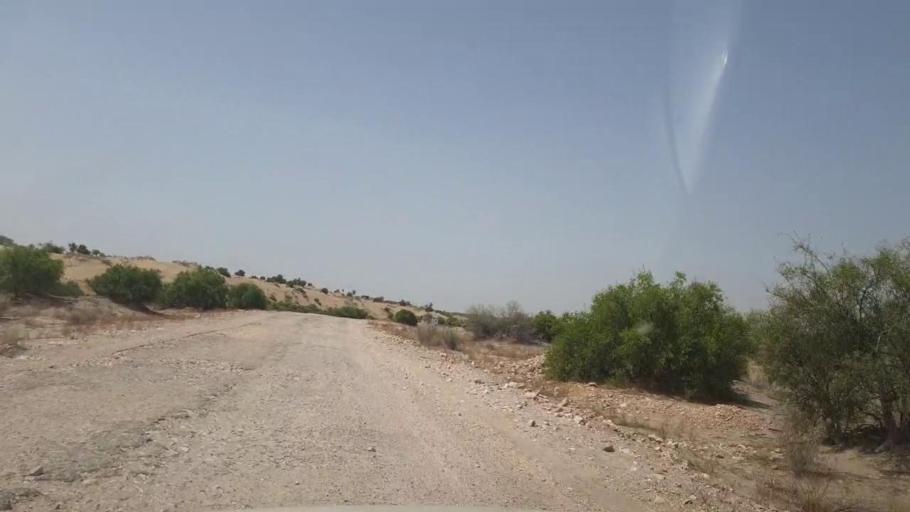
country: PK
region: Sindh
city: Khanpur
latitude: 27.3692
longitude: 69.3179
